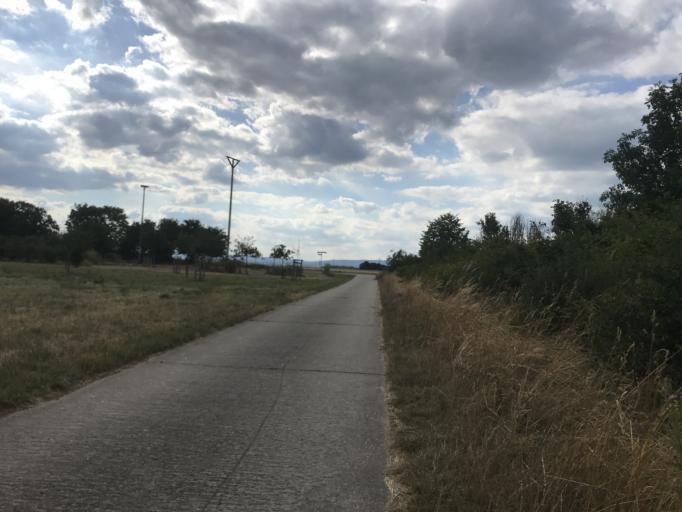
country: DE
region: Hesse
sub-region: Regierungsbezirk Darmstadt
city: Hochheim am Main
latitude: 50.0254
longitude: 8.3279
